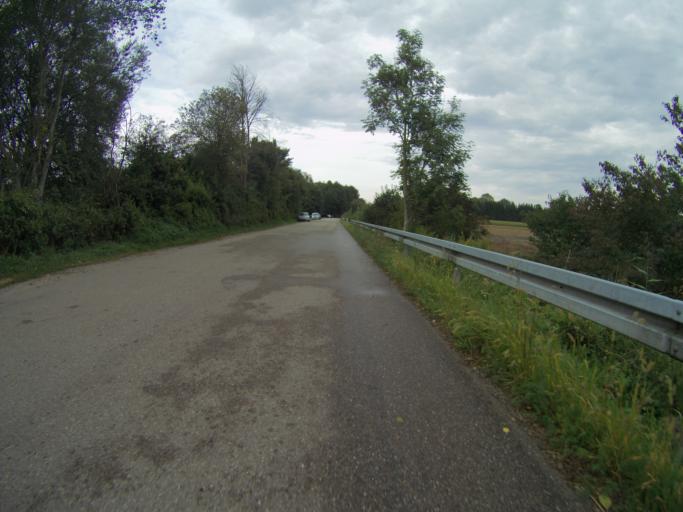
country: DE
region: Bavaria
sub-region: Upper Bavaria
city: Marzling
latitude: 48.3924
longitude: 11.8023
